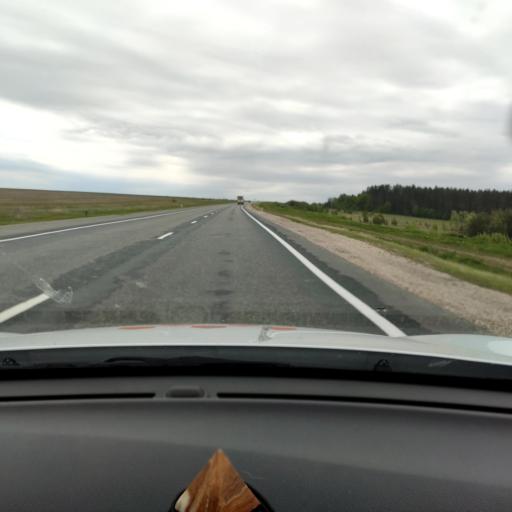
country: RU
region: Tatarstan
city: Laishevo
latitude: 55.5040
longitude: 49.8286
